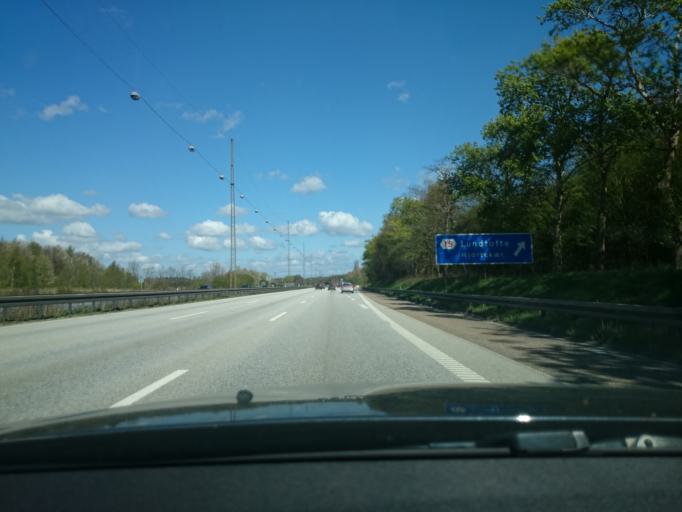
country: DK
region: Capital Region
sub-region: Lyngby-Tarbaek Kommune
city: Kongens Lyngby
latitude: 55.7925
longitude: 12.5310
